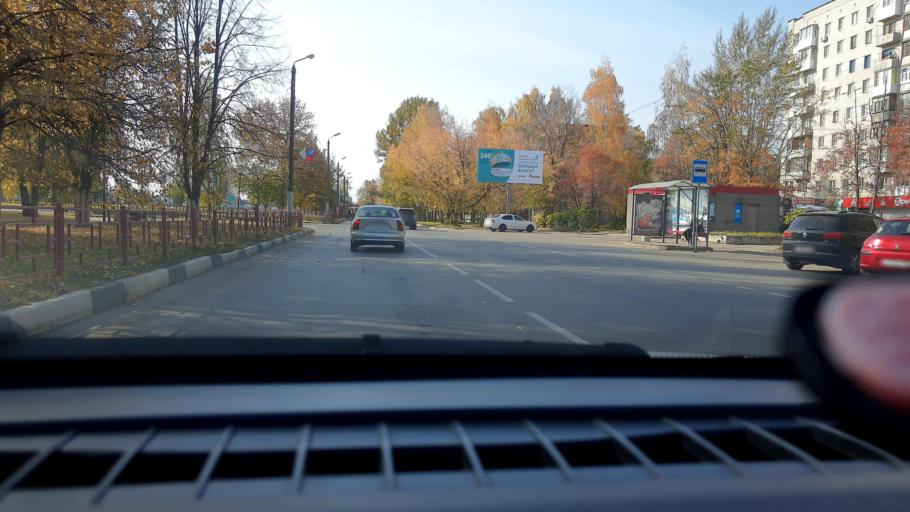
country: RU
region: Nizjnij Novgorod
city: Kstovo
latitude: 56.1422
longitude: 44.1888
